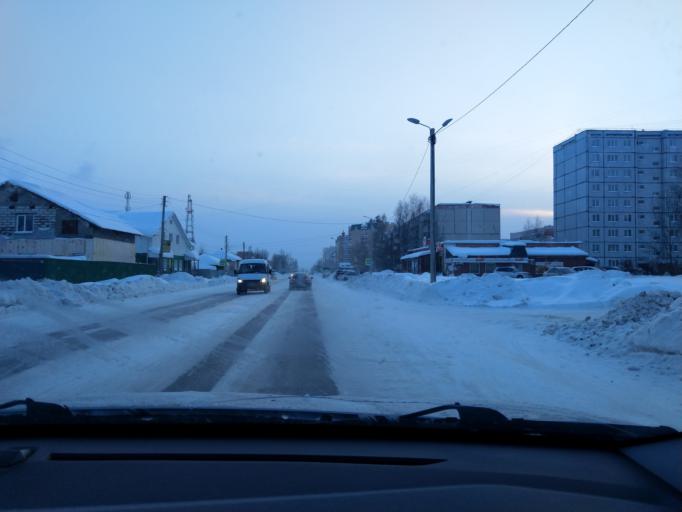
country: RU
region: Perm
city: Dobryanka
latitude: 58.4703
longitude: 56.4060
